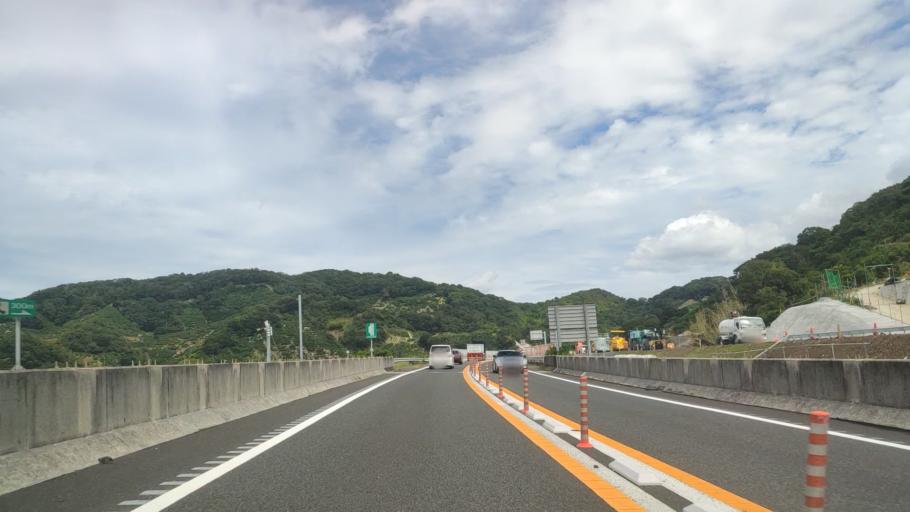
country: JP
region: Wakayama
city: Kainan
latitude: 34.0171
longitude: 135.1915
